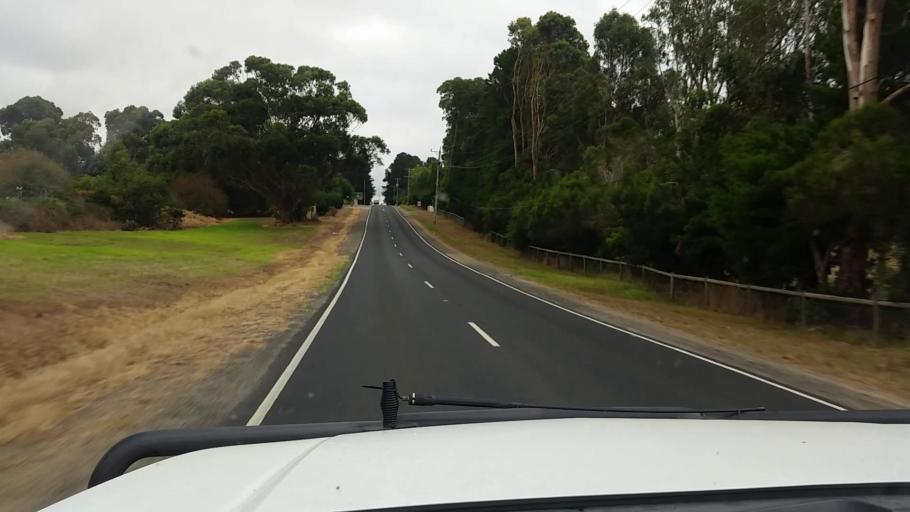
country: AU
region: Victoria
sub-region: Mornington Peninsula
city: Hastings
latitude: -38.2892
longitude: 145.1456
